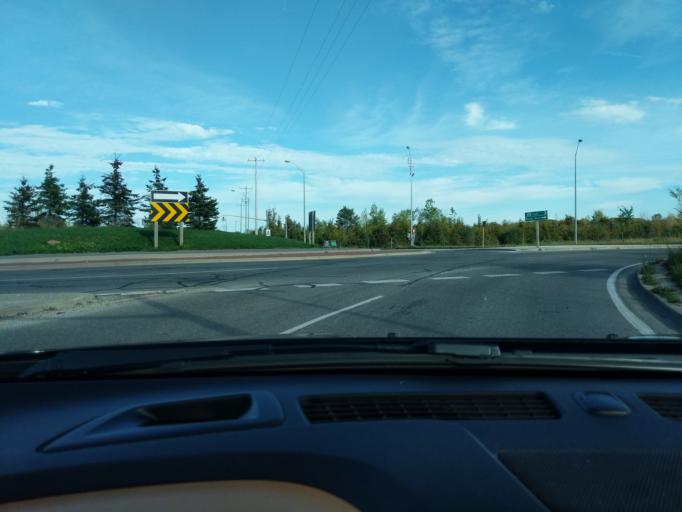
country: CA
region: Ontario
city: Collingwood
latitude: 44.4870
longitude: -80.1743
